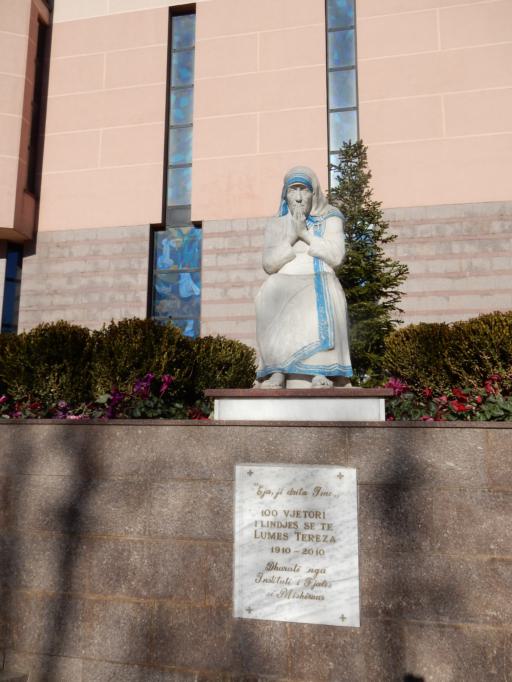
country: AL
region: Tirane
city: Tirana
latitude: 41.3247
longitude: 19.8222
